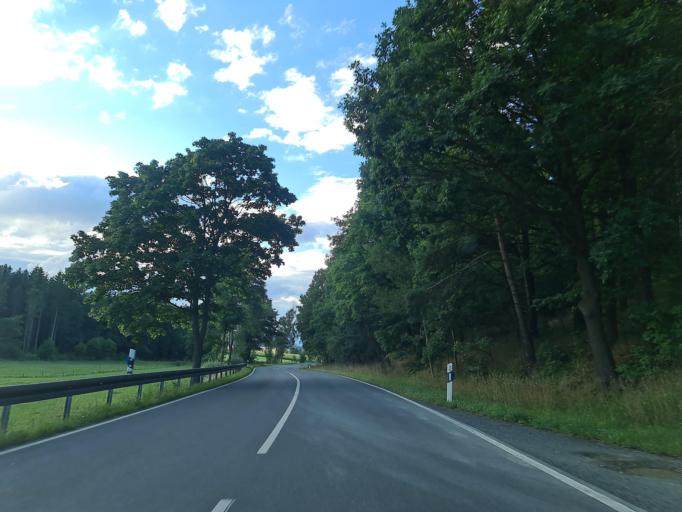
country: DE
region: Saxony
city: Mehltheuer
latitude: 50.5547
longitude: 12.0102
